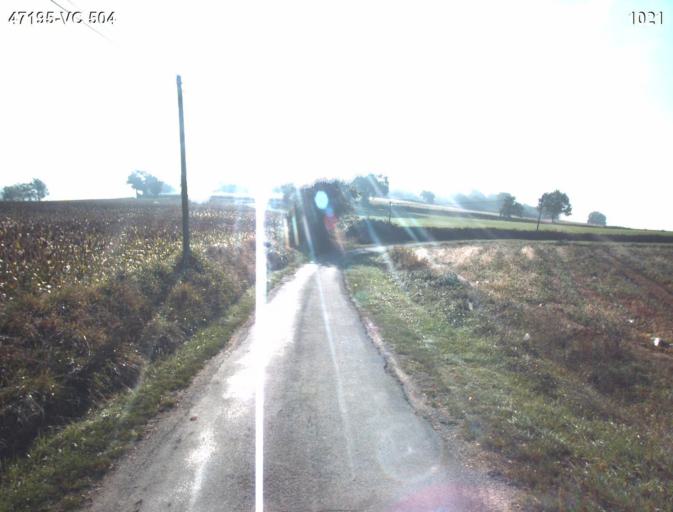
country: FR
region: Aquitaine
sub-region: Departement du Lot-et-Garonne
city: Nerac
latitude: 44.1561
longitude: 0.3337
